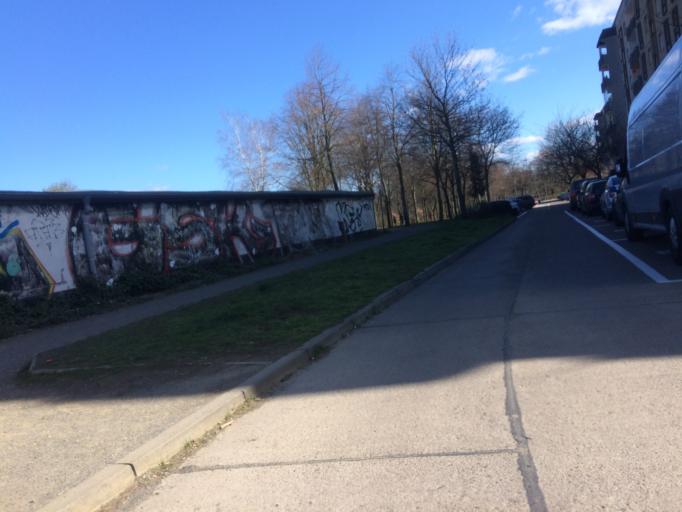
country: DE
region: Berlin
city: Weissensee
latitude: 52.5505
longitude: 13.4773
